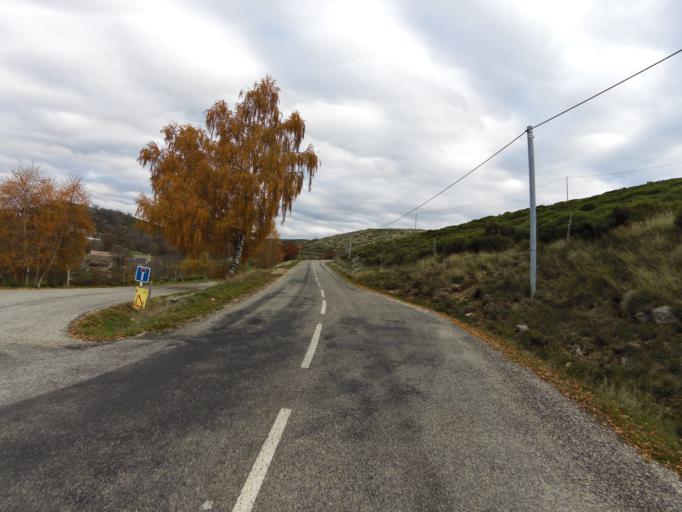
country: FR
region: Rhone-Alpes
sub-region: Departement de l'Ardeche
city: Les Vans
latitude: 44.5342
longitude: 4.0206
